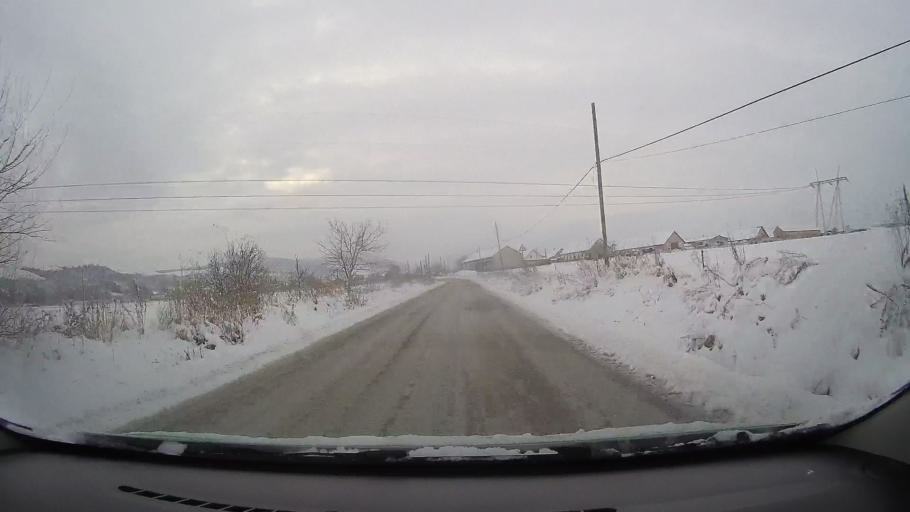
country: RO
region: Alba
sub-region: Comuna Pianu
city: Pianu de Jos
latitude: 45.9491
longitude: 23.4787
